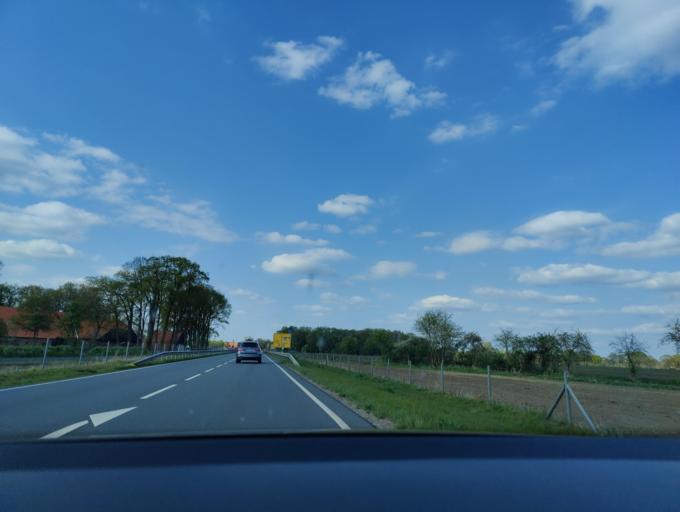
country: DE
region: Lower Saxony
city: Nordhorn
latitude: 52.4535
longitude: 7.0894
